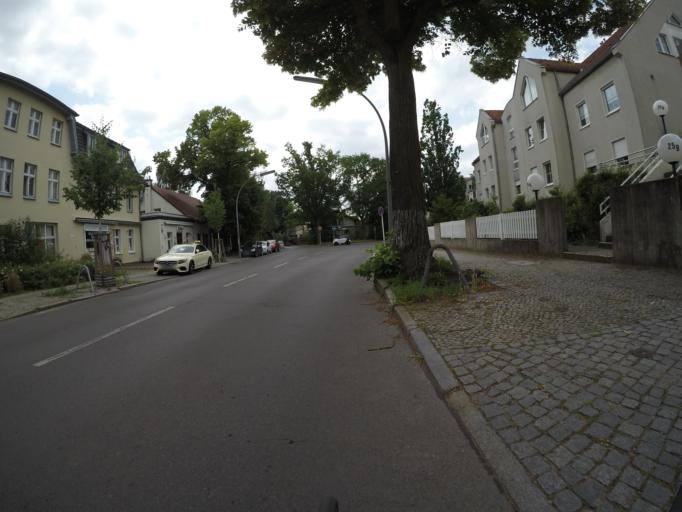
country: DE
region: Berlin
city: Wannsee
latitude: 52.4142
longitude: 13.1441
